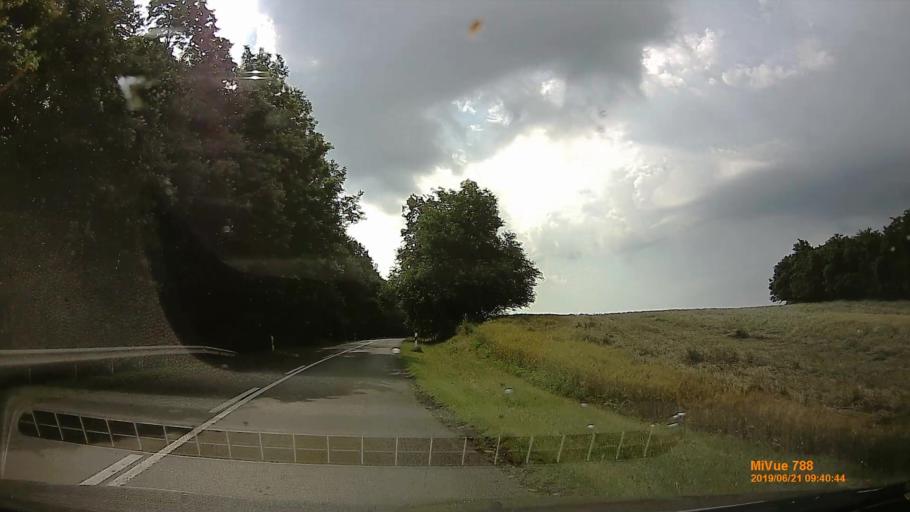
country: HU
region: Somogy
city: Taszar
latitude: 46.2946
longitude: 17.9473
